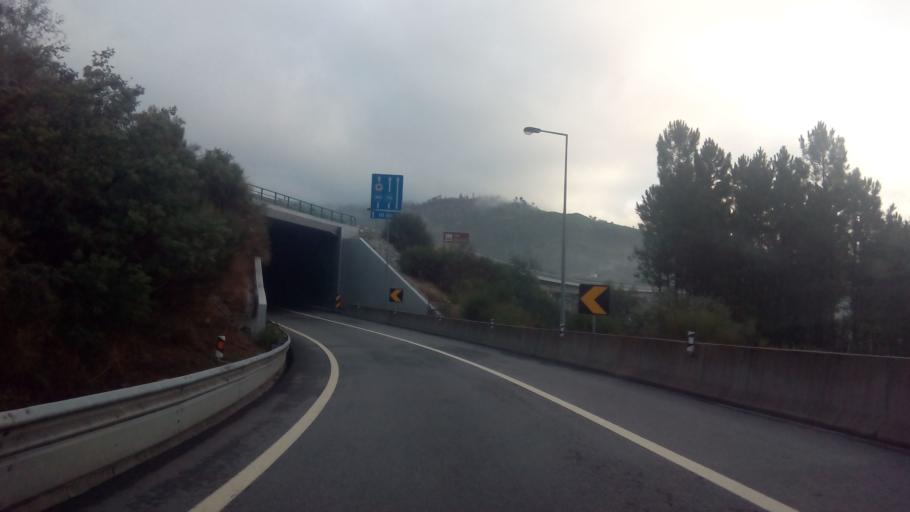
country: PT
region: Porto
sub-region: Amarante
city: Amarante
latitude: 41.2588
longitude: -8.0318
